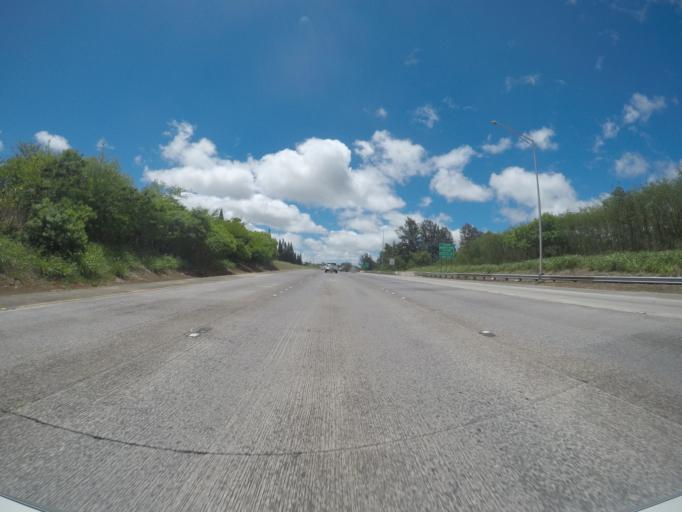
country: US
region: Hawaii
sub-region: Honolulu County
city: Waipio
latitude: 21.4222
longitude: -157.9944
